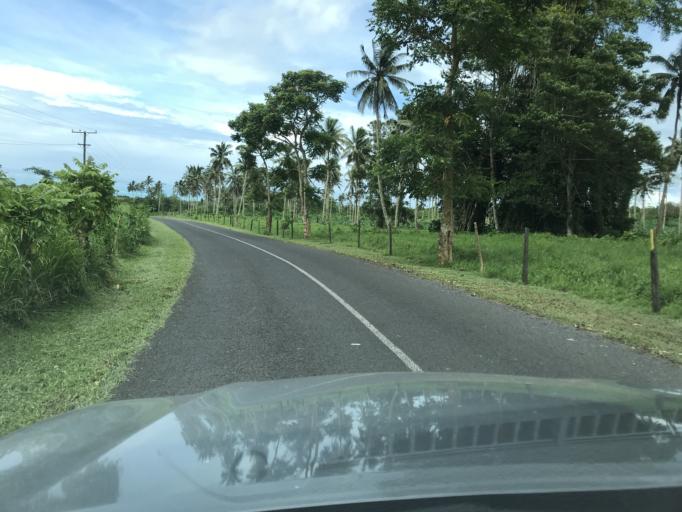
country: WS
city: Fasito`outa
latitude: -13.8699
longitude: -171.9130
